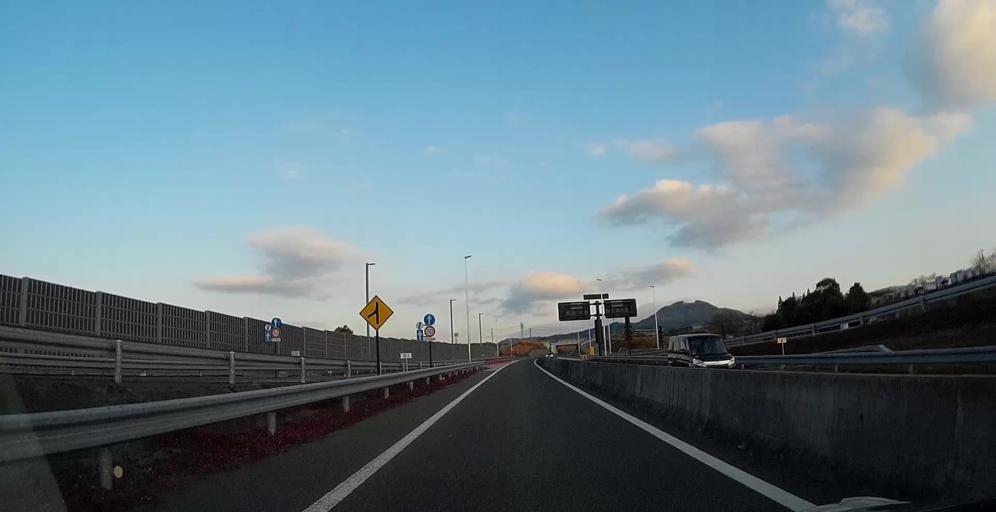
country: JP
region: Kumamoto
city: Kumamoto
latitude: 32.7540
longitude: 130.7898
